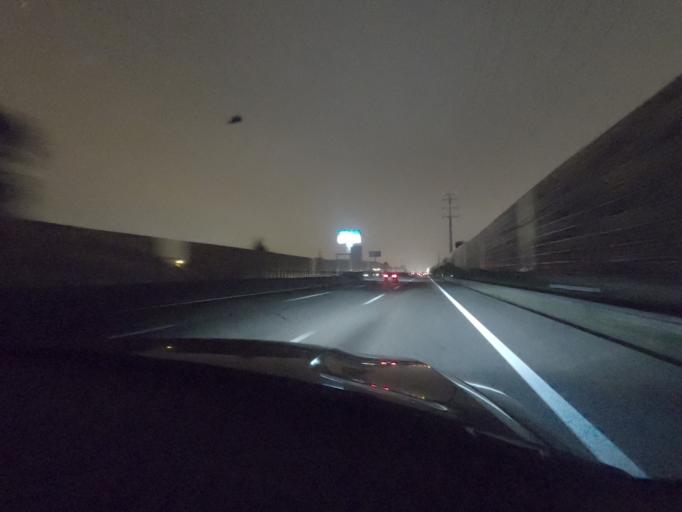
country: PT
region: Lisbon
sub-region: Loures
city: Sao Joao da Talha
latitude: 38.8287
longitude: -9.0979
